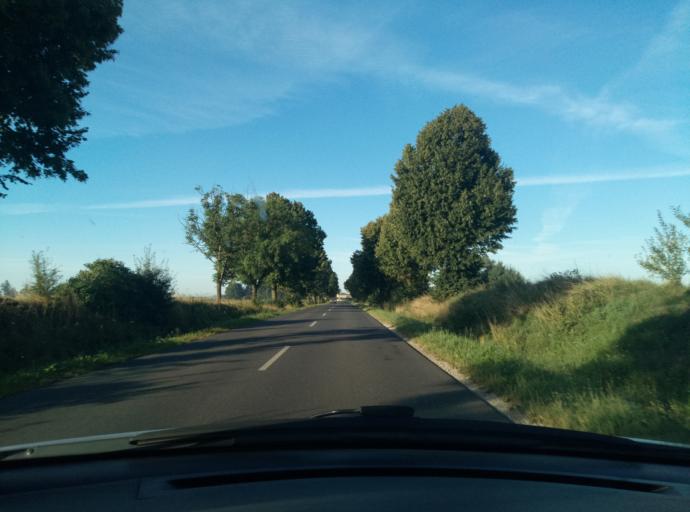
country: PL
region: Kujawsko-Pomorskie
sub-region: Powiat golubsko-dobrzynski
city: Kowalewo Pomorskie
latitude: 53.2073
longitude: 18.9219
